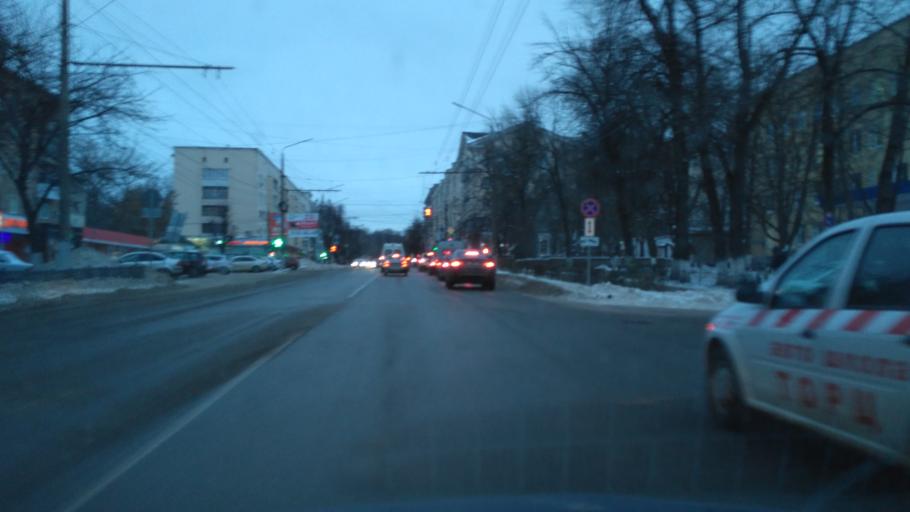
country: RU
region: Tula
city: Tula
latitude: 54.1829
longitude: 37.6001
